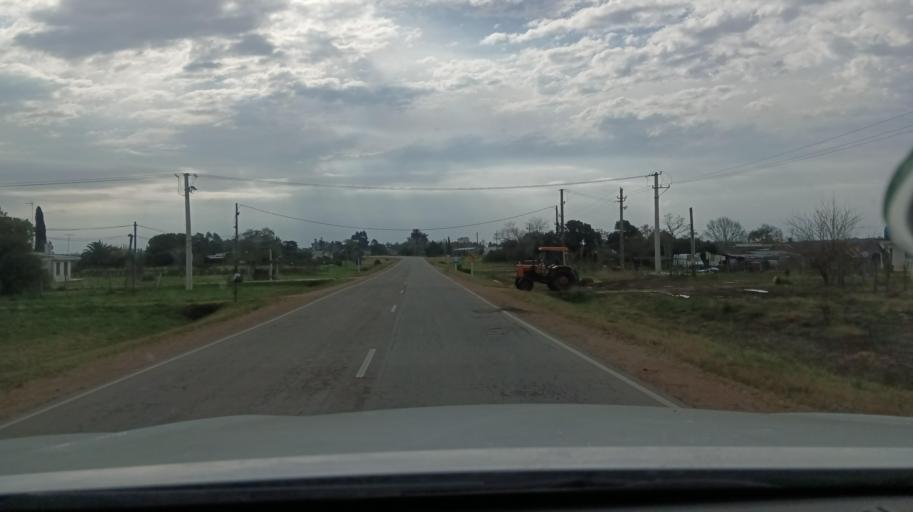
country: UY
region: Canelones
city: Toledo
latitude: -34.6931
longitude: -56.1077
